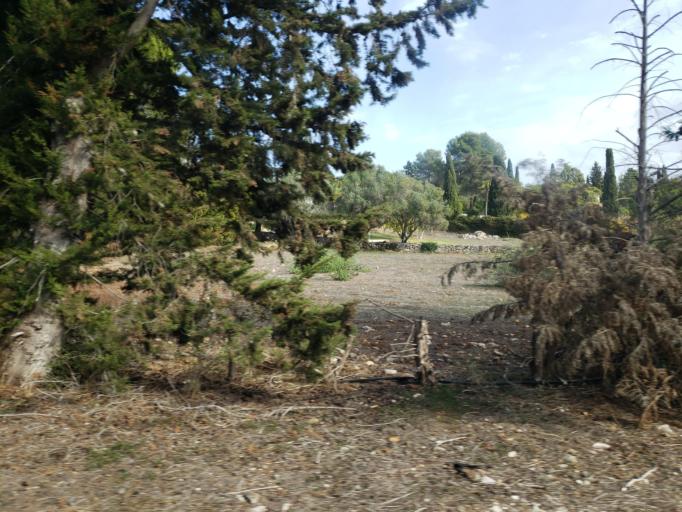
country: PT
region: Faro
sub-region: Portimao
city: Alvor
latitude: 37.1841
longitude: -8.5854
